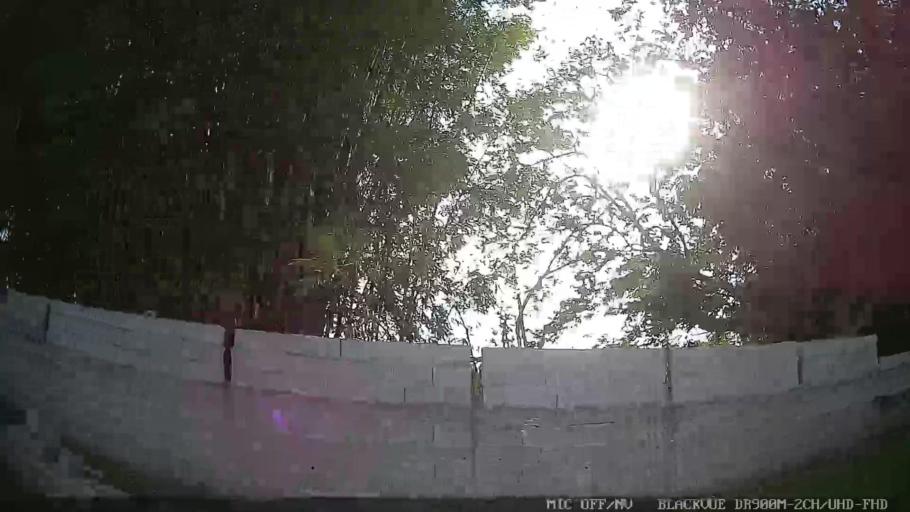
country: BR
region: Sao Paulo
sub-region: Peruibe
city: Peruibe
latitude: -24.2717
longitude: -46.9380
